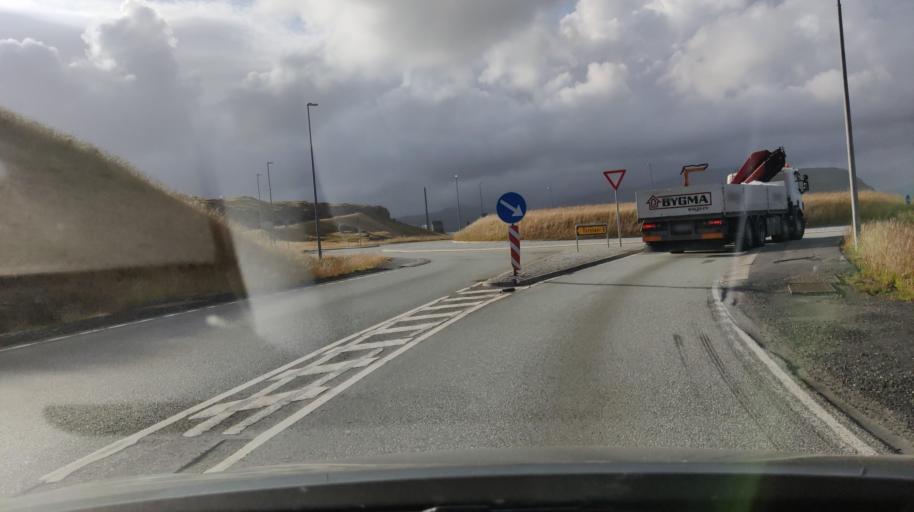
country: FO
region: Streymoy
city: Hoyvik
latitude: 62.0439
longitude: -6.7787
